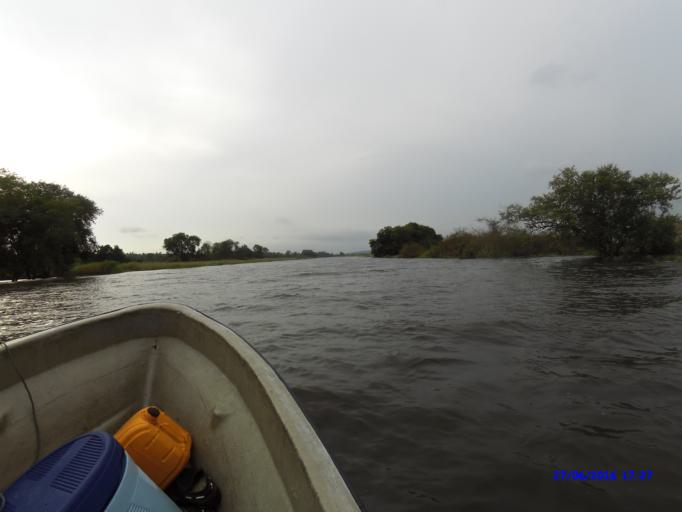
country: BJ
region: Atlantique
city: Allada
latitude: 6.6026
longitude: 1.9782
